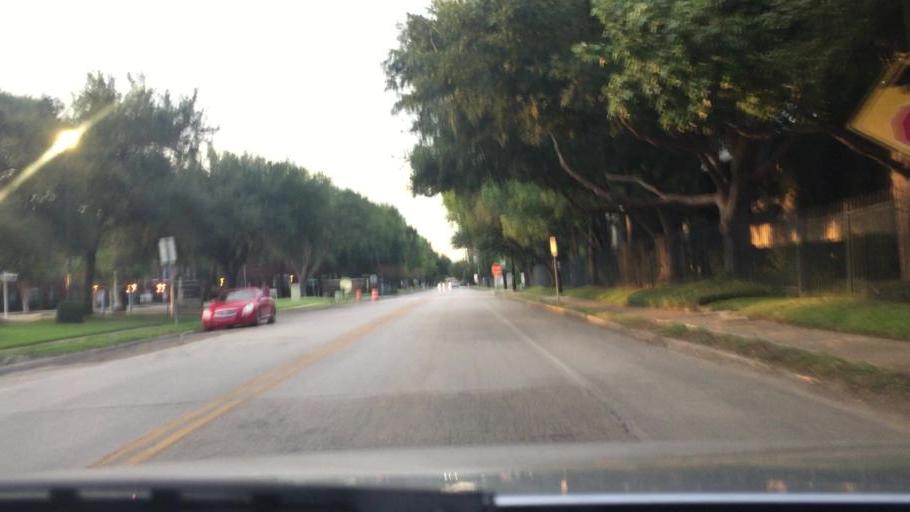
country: US
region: Texas
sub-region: Harris County
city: Hunters Creek Village
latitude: 29.7559
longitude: -95.4796
